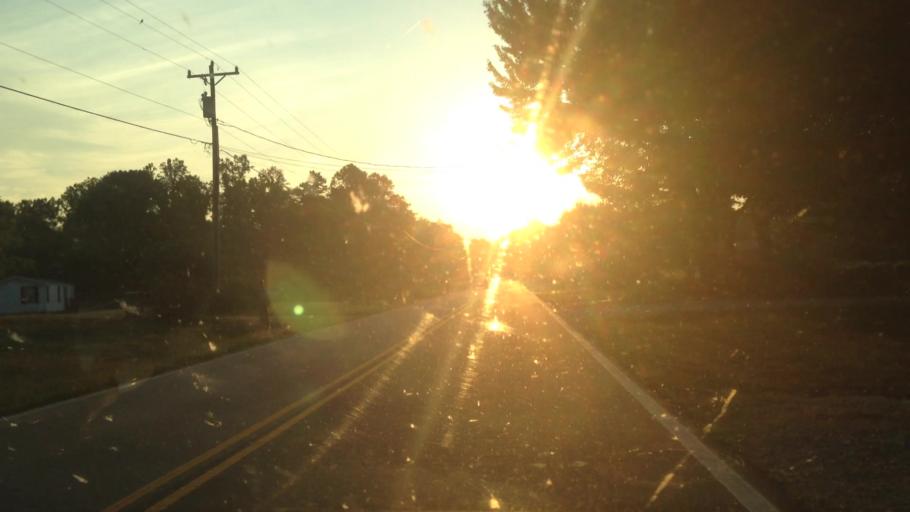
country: US
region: North Carolina
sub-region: Forsyth County
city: Walkertown
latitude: 36.1576
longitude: -80.1217
